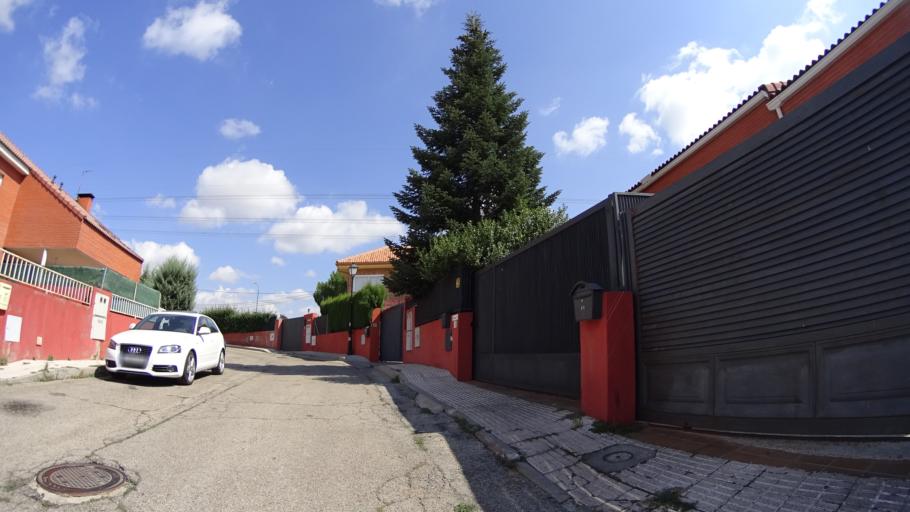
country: ES
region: Madrid
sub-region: Provincia de Madrid
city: Galapagar
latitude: 40.5821
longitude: -3.9943
